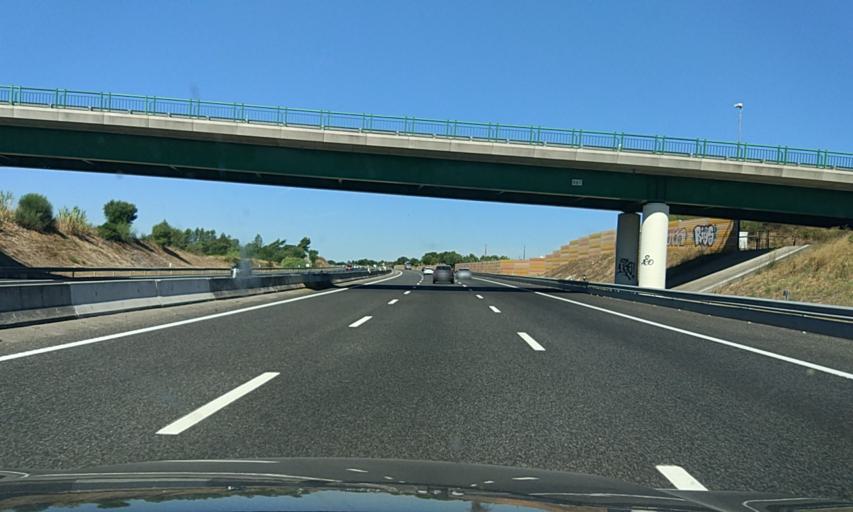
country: PT
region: Santarem
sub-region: Cartaxo
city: Pontevel
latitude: 39.1786
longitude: -8.8362
